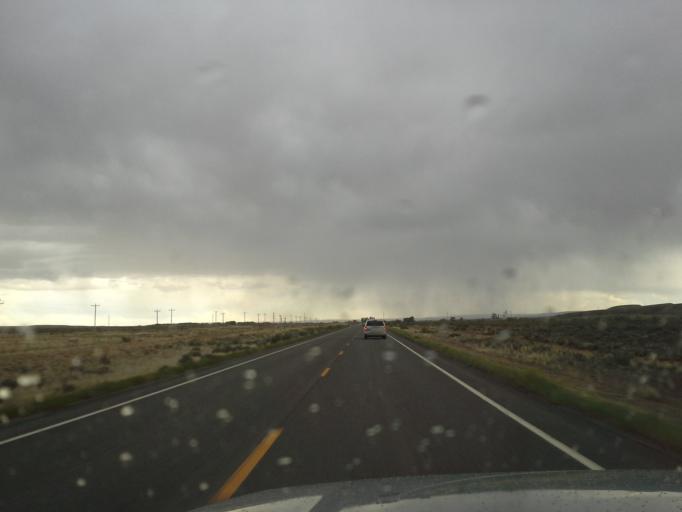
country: US
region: Wyoming
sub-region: Park County
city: Powell
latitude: 45.0207
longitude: -108.6302
